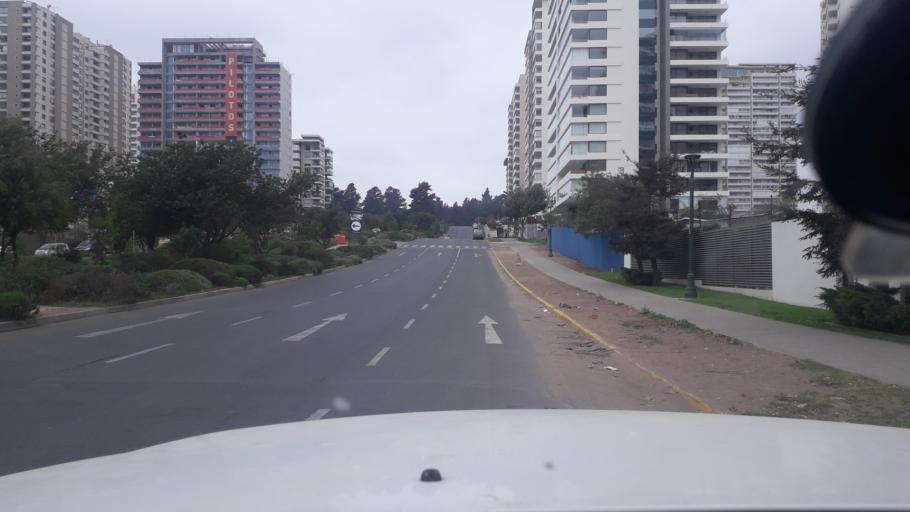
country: CL
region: Valparaiso
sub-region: Provincia de Valparaiso
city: Vina del Mar
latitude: -32.9492
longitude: -71.5426
